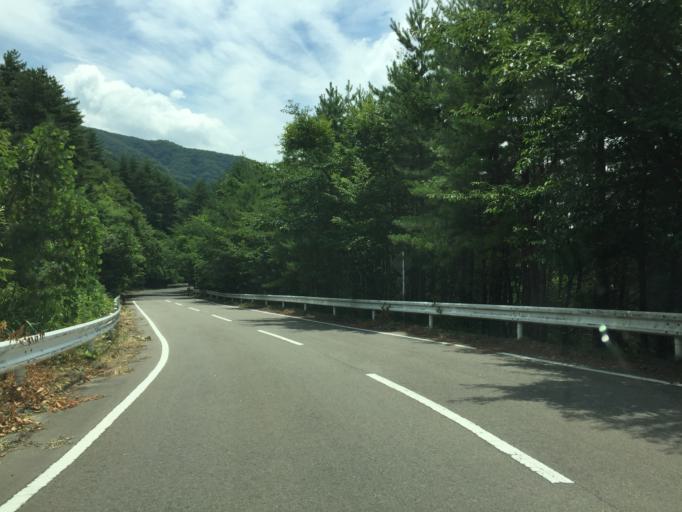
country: JP
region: Fukushima
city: Hobaramachi
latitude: 37.6757
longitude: 140.6574
